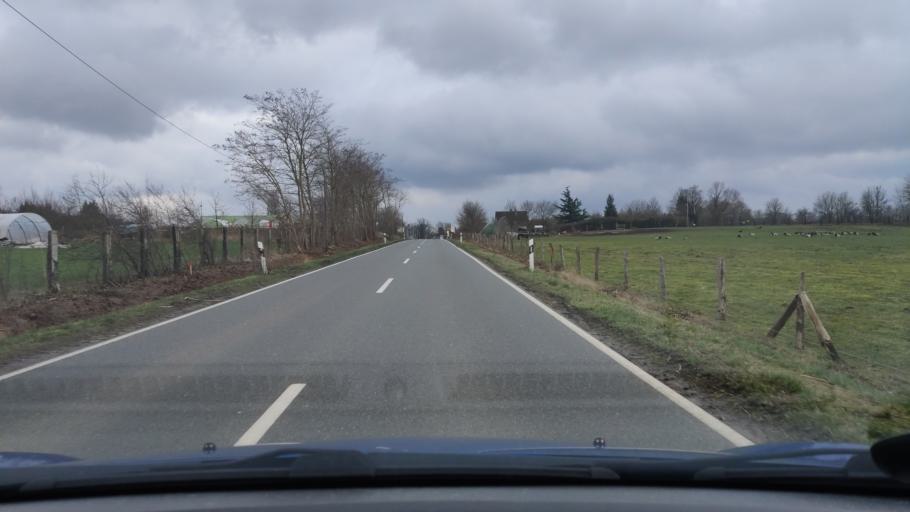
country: DE
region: Lower Saxony
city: Garbsen-Mitte
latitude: 52.4517
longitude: 9.6514
